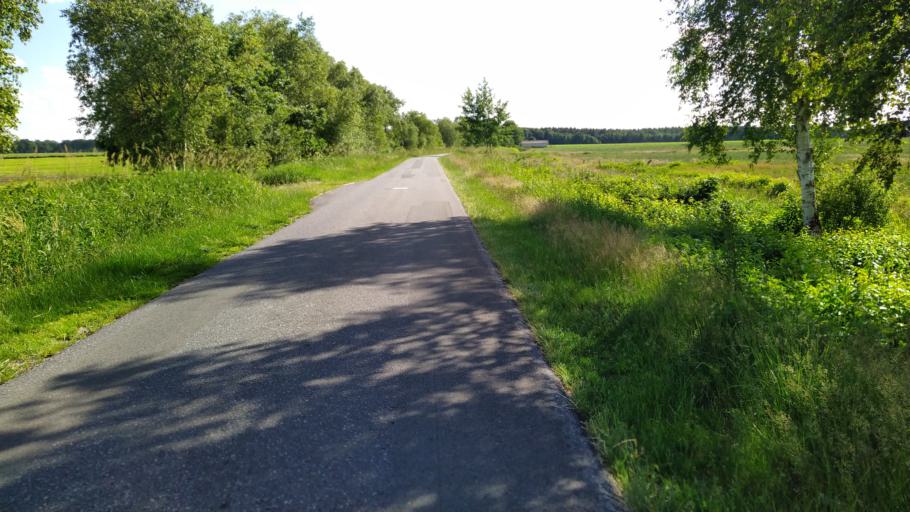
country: DE
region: Lower Saxony
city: Steinau
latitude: 53.6453
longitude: 8.9080
